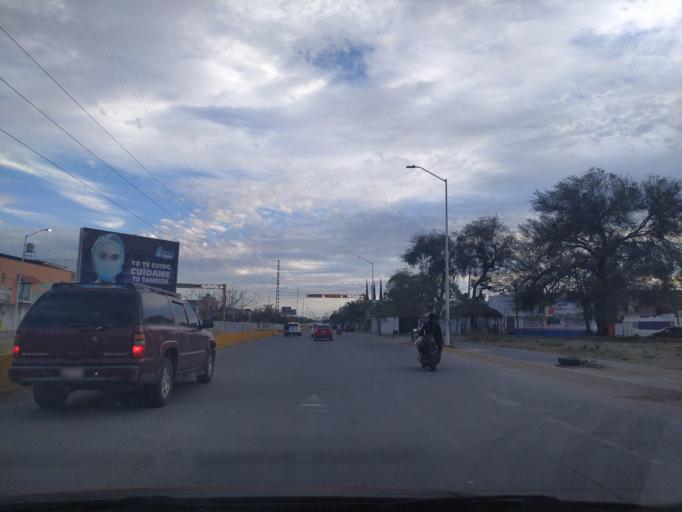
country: LA
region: Oudomxai
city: Muang La
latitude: 21.0278
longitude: 101.8695
